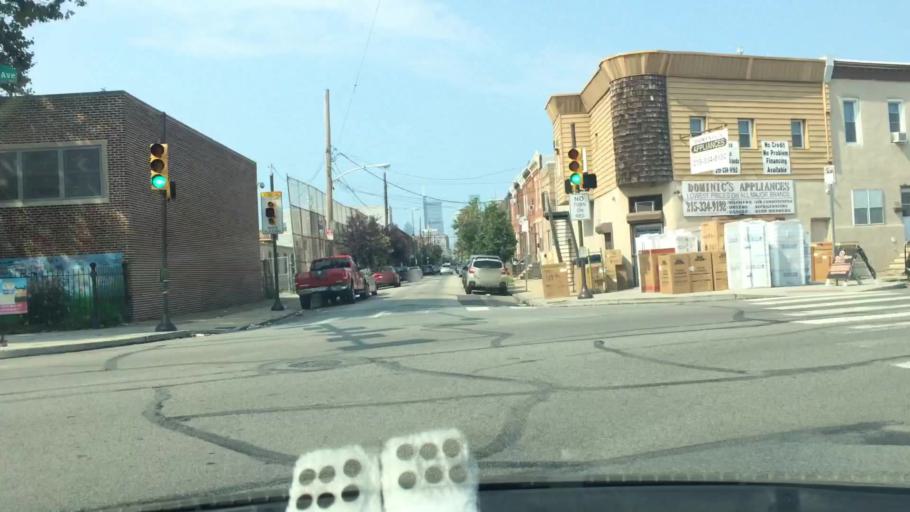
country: US
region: Pennsylvania
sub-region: Philadelphia County
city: Philadelphia
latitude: 39.9242
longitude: -75.1763
